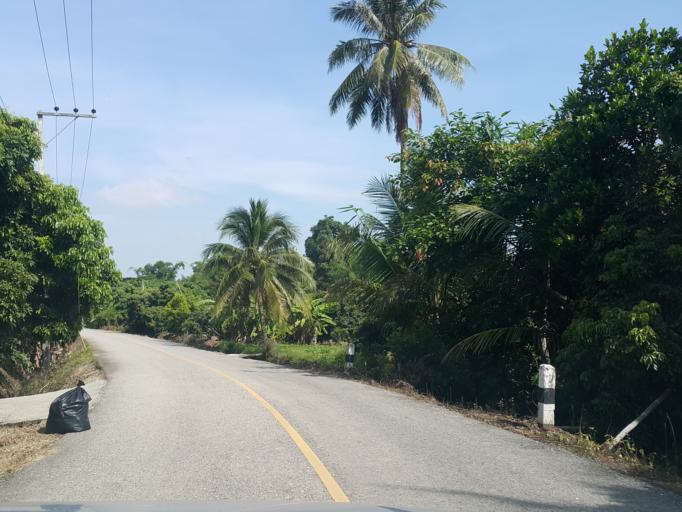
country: TH
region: Chiang Mai
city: Saraphi
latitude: 18.6885
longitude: 99.0745
